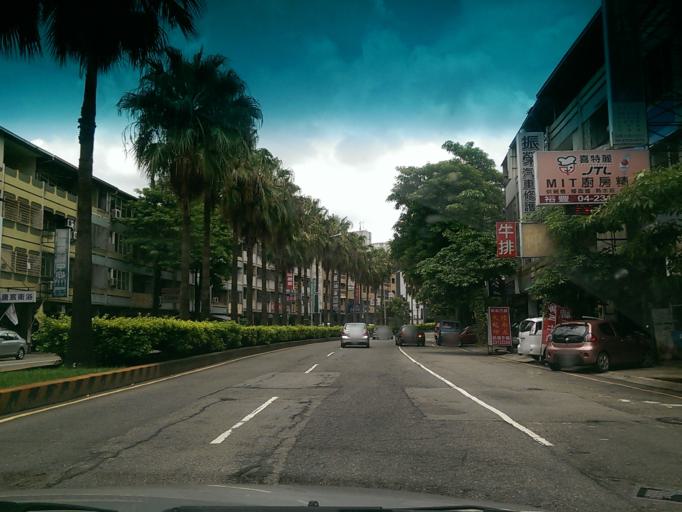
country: TW
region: Taiwan
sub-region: Taichung City
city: Taichung
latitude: 24.1601
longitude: 120.6618
